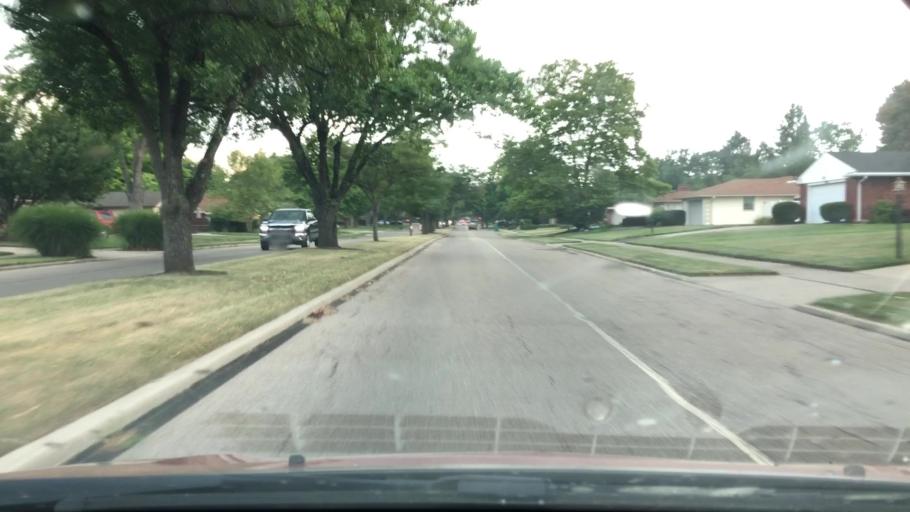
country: US
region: Ohio
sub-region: Montgomery County
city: Centerville
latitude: 39.6625
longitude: -84.1207
